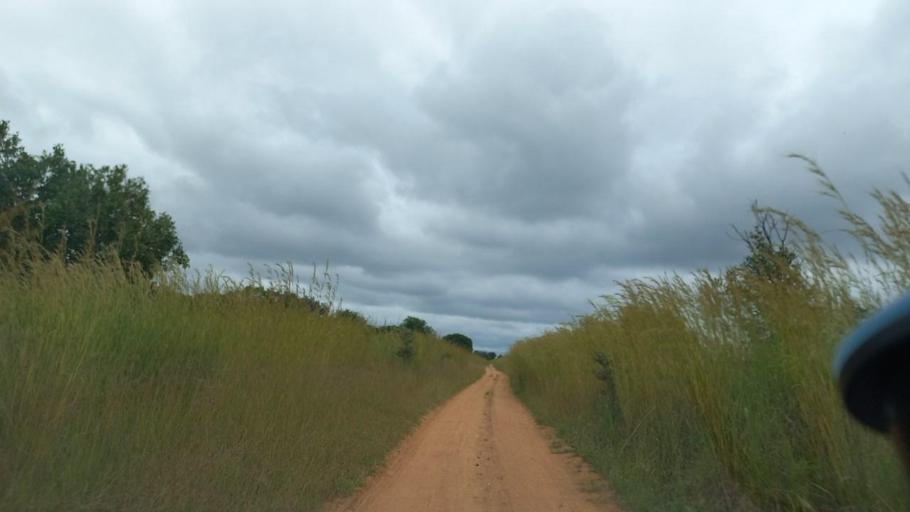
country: ZM
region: Lusaka
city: Lusaka
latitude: -15.1295
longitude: 28.3698
